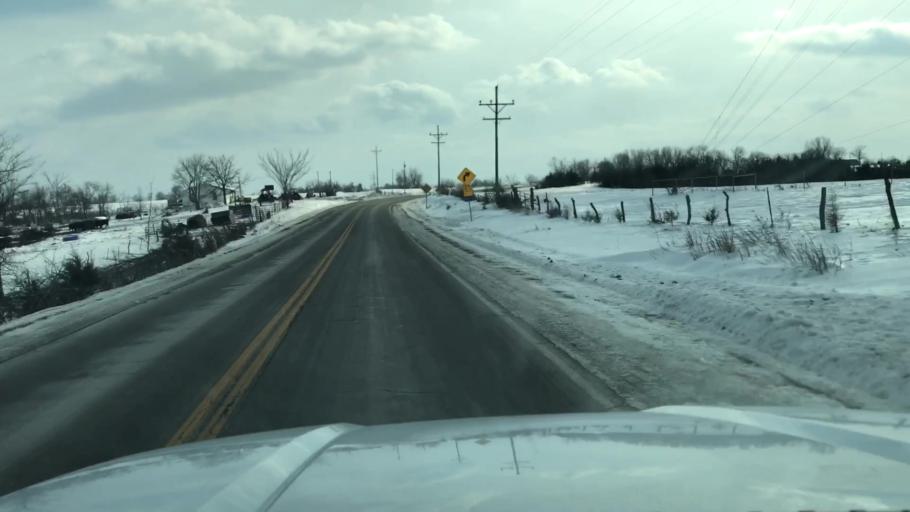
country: US
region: Missouri
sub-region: Gentry County
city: Stanberry
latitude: 40.3705
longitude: -94.6474
